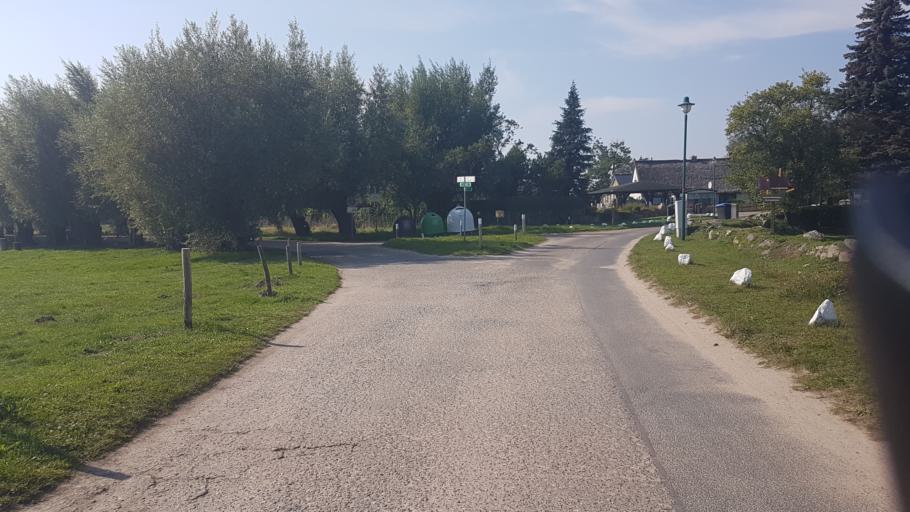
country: DE
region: Mecklenburg-Vorpommern
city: Putbus
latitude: 54.3358
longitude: 13.4844
